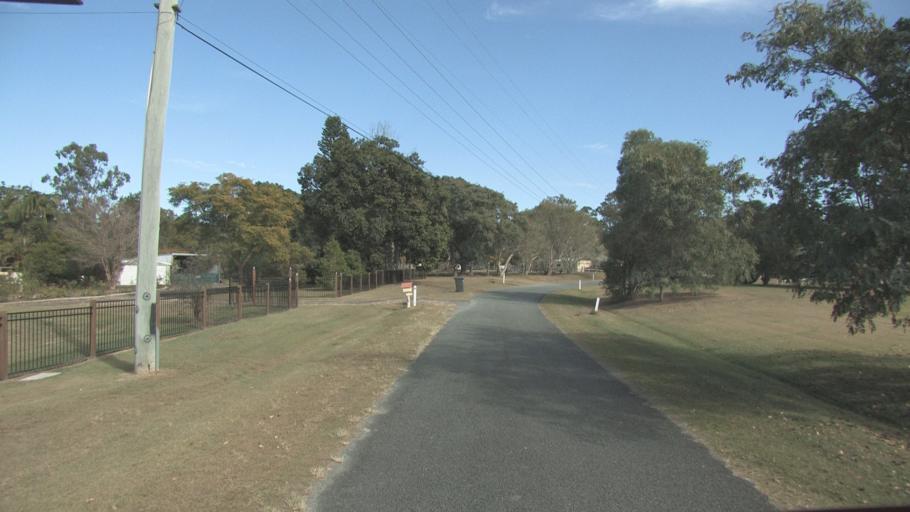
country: AU
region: Queensland
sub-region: Logan
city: North Maclean
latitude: -27.7761
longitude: 152.9955
